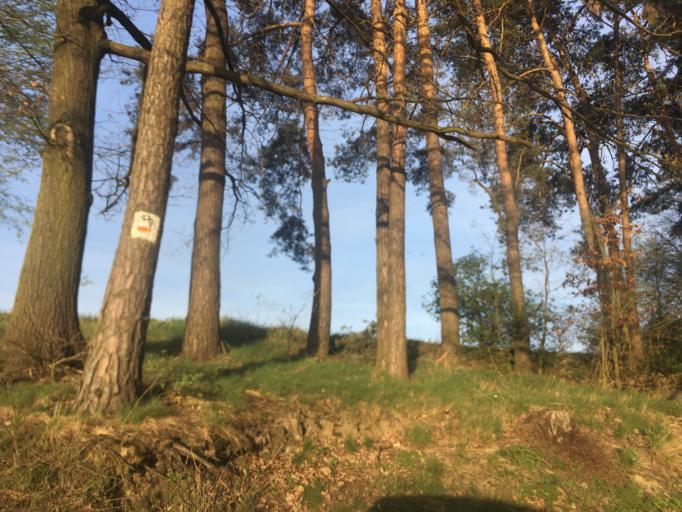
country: PL
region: Kujawsko-Pomorskie
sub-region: Powiat brodnicki
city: Gorzno
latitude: 53.2067
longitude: 19.6648
